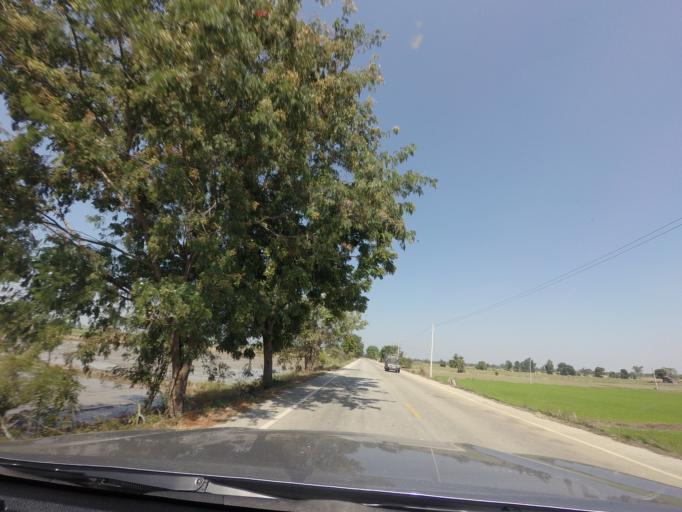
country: TH
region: Sukhothai
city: Sukhothai
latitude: 17.0846
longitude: 99.7907
